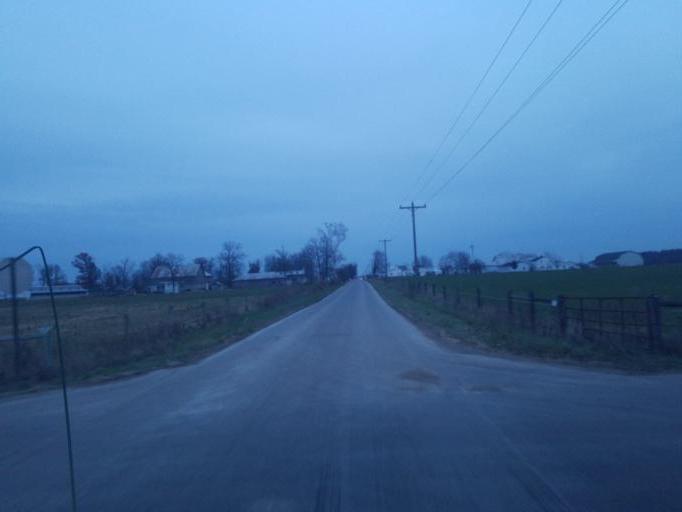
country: US
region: Indiana
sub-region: Adams County
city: Berne
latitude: 40.7313
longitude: -84.9175
